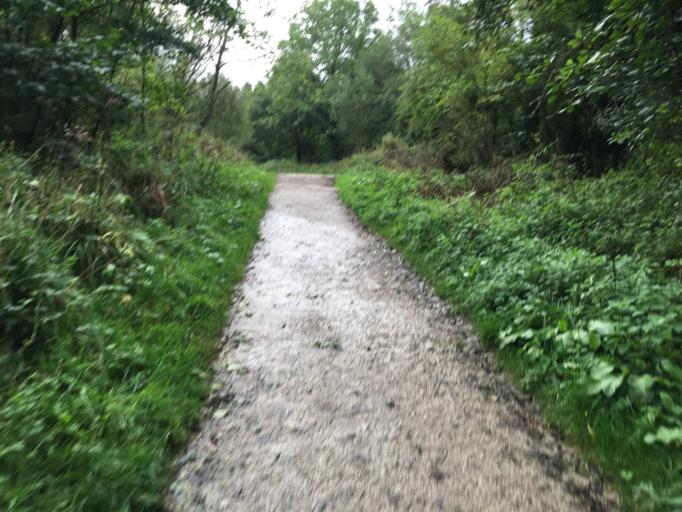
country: GB
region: England
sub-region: North Yorkshire
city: Sleights
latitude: 54.4044
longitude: -0.7260
